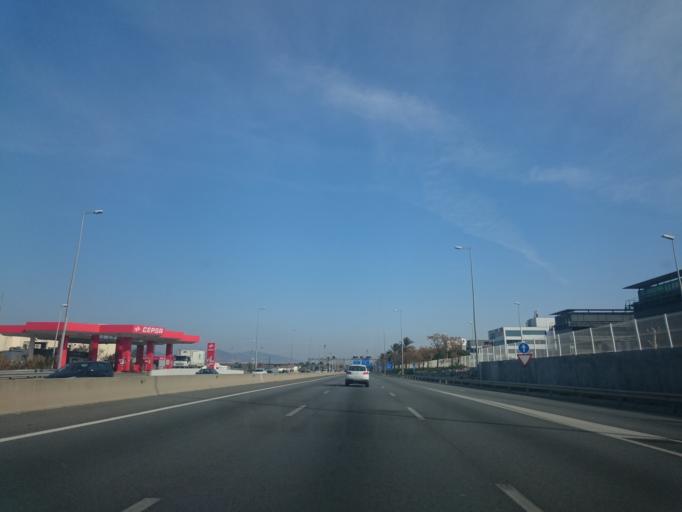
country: ES
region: Catalonia
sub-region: Provincia de Barcelona
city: El Prat de Llobregat
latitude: 41.3156
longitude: 2.0699
